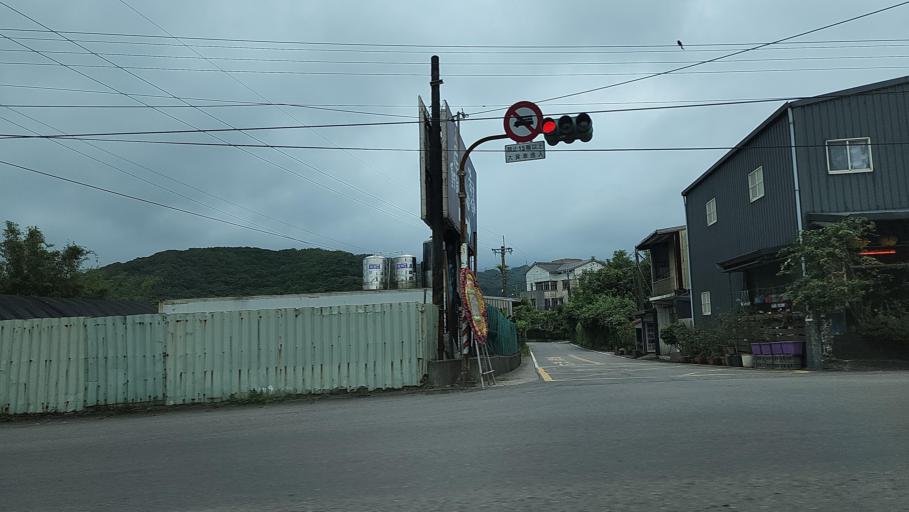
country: TW
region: Taiwan
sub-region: Keelung
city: Keelung
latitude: 25.2121
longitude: 121.6468
